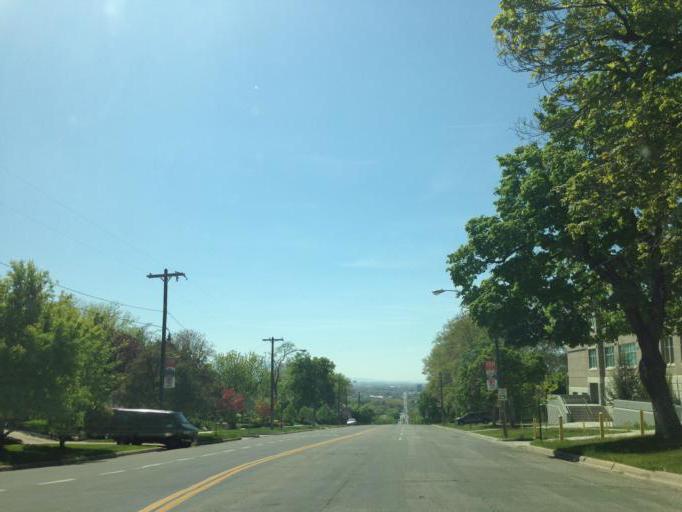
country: US
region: Utah
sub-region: Salt Lake County
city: Salt Lake City
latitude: 40.7498
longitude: -111.8543
